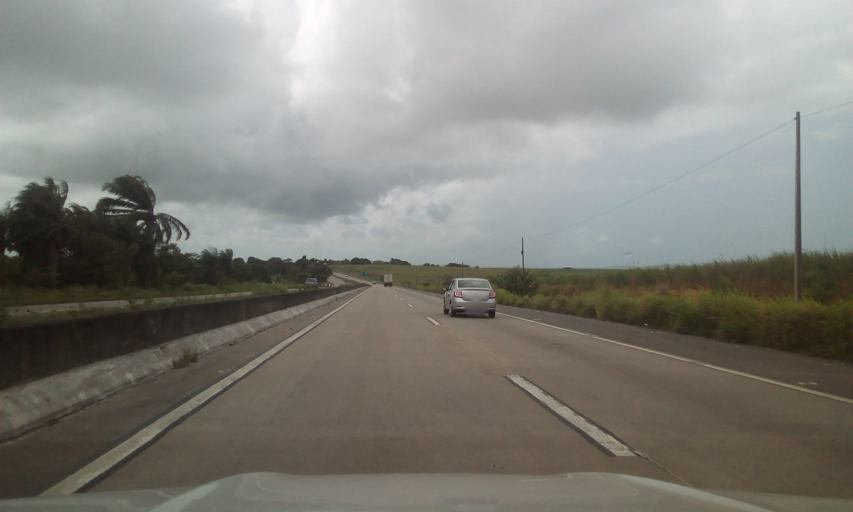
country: BR
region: Pernambuco
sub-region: Itapissuma
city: Itapissuma
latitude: -7.7108
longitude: -34.9307
